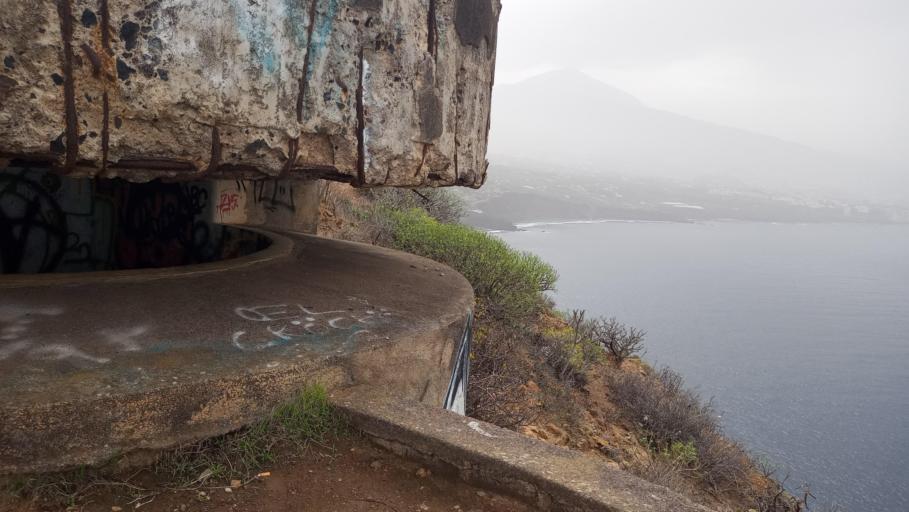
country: ES
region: Canary Islands
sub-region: Provincia de Santa Cruz de Tenerife
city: Santa Ursula
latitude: 28.4370
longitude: -16.4966
